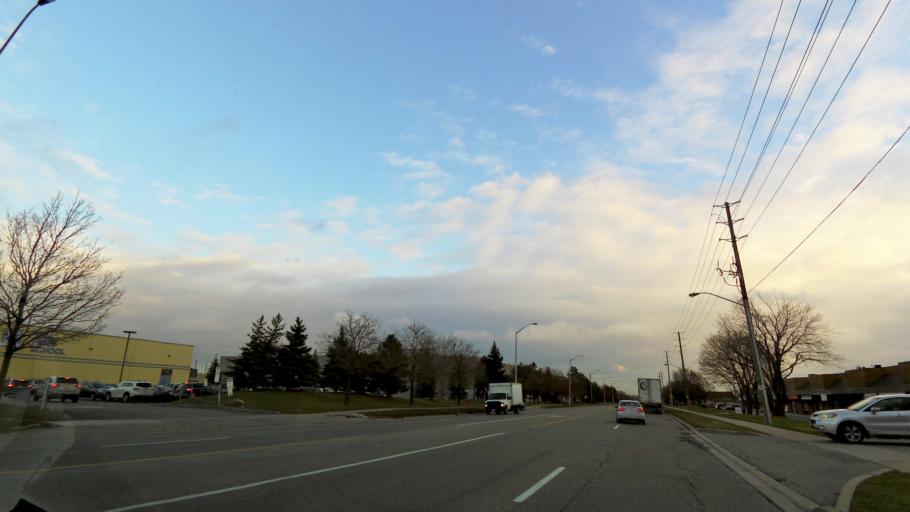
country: CA
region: Ontario
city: Brampton
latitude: 43.7246
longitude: -79.6940
